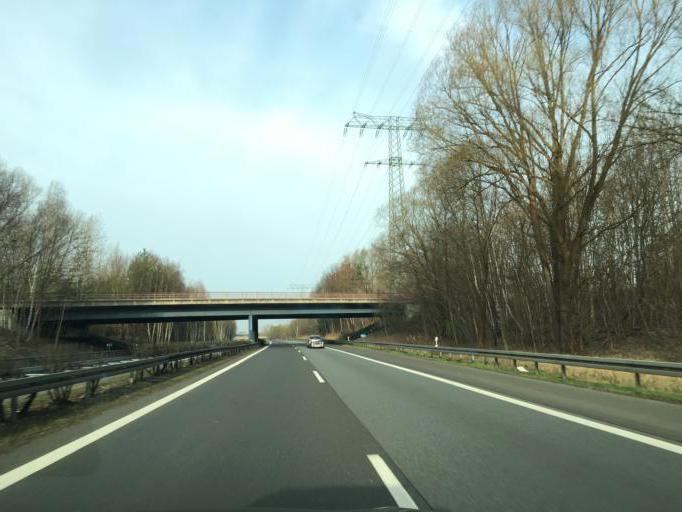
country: DE
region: Brandenburg
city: Birkenwerder
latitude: 52.7000
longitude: 13.2765
